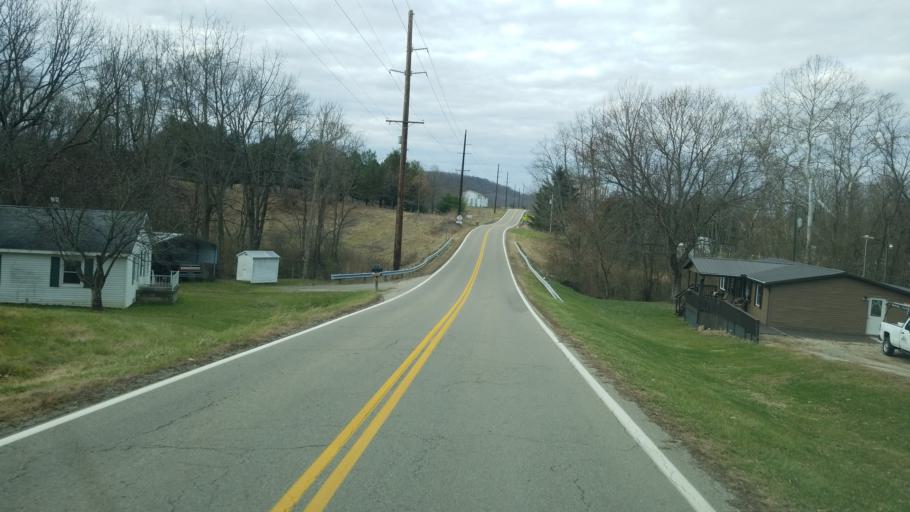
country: US
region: Ohio
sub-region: Ross County
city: Frankfort
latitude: 39.3480
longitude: -83.2055
